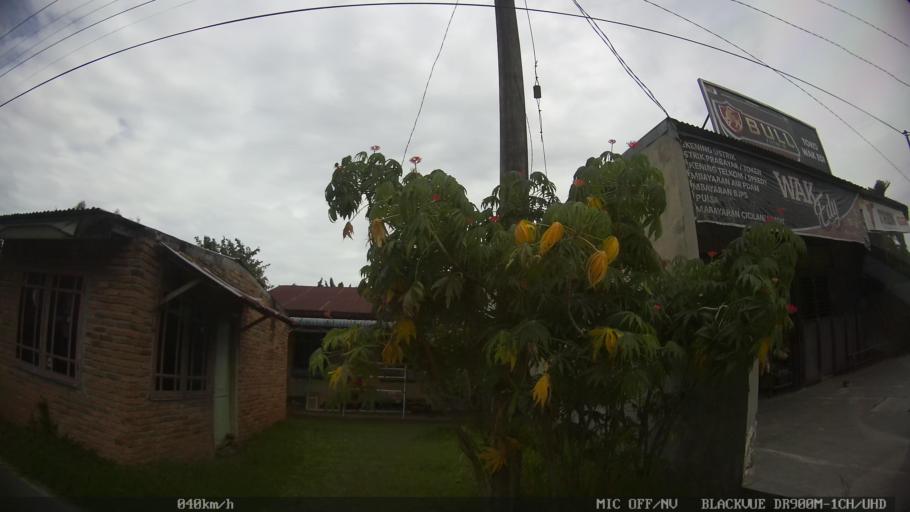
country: ID
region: North Sumatra
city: Sunggal
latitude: 3.6199
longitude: 98.5930
